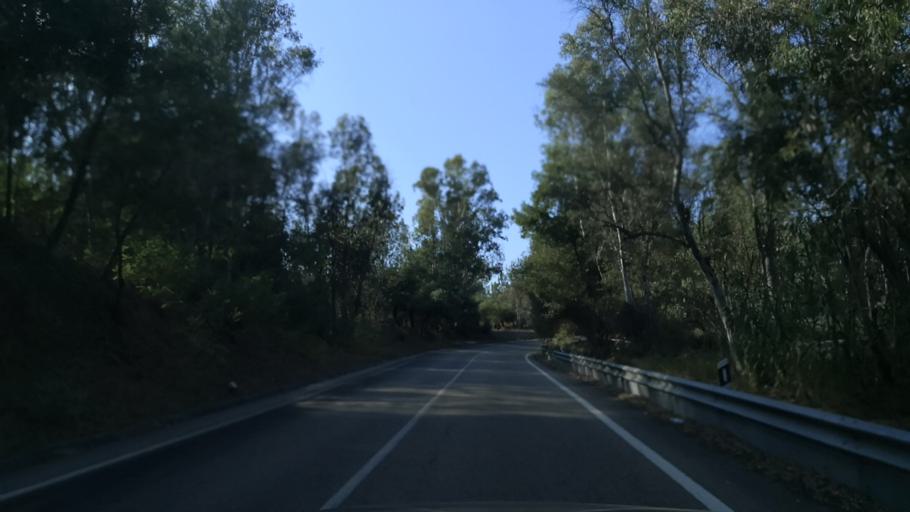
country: PT
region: Santarem
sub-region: Almeirim
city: Fazendas de Almeirim
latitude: 39.0673
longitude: -8.5654
